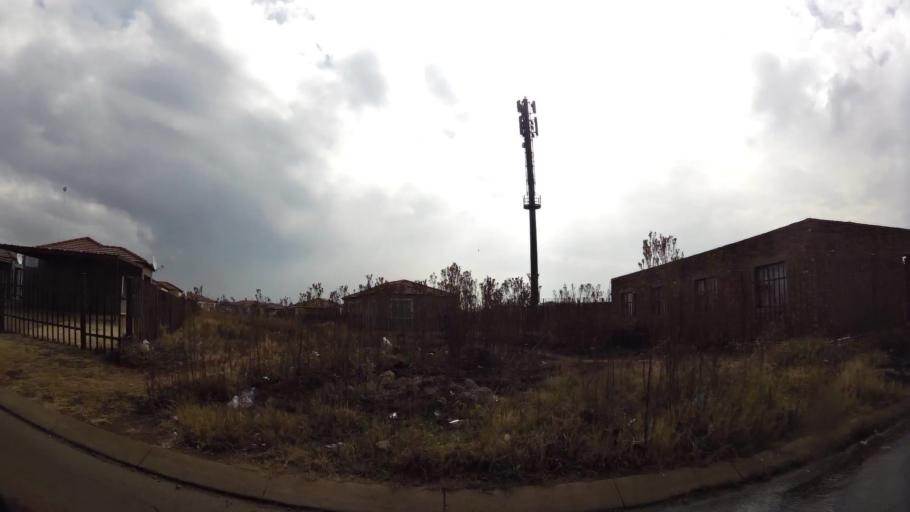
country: ZA
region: Gauteng
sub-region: Sedibeng District Municipality
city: Vanderbijlpark
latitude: -26.7162
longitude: 27.8834
